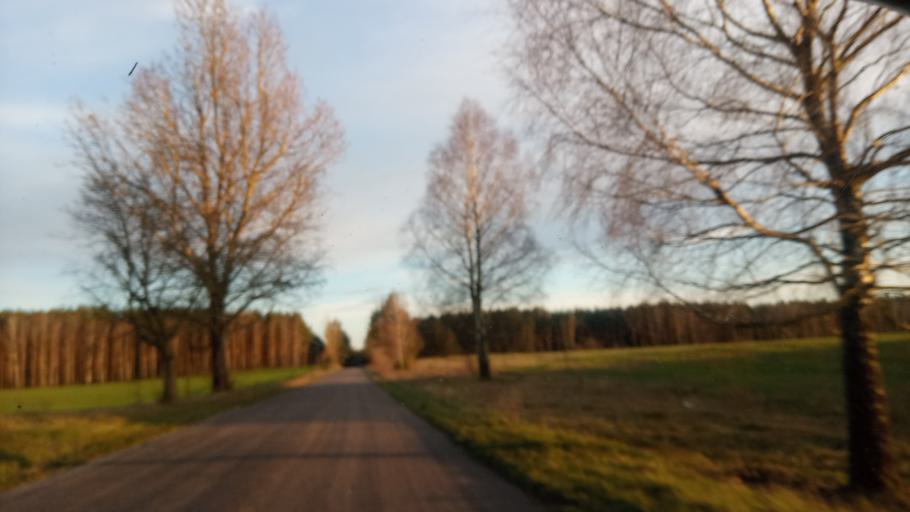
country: PL
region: West Pomeranian Voivodeship
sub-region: Powiat szczecinecki
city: Lubowo
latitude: 53.5784
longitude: 16.3949
